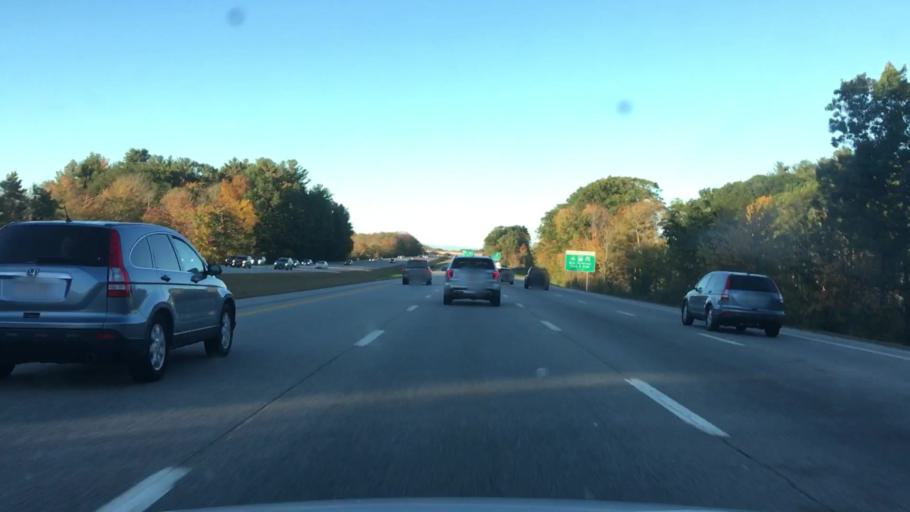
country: US
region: New Hampshire
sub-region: Rockingham County
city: Greenland
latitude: 43.0327
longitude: -70.8223
